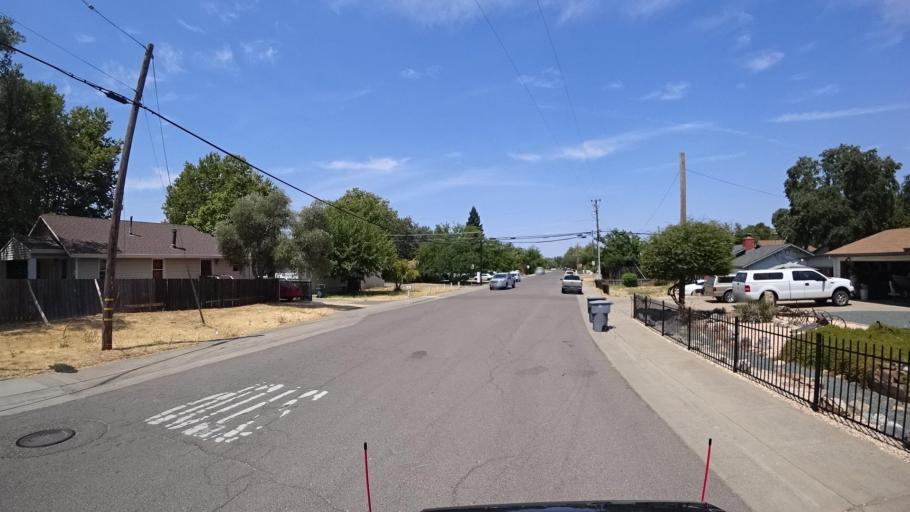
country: US
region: California
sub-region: Placer County
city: Rocklin
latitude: 38.7916
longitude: -121.2307
